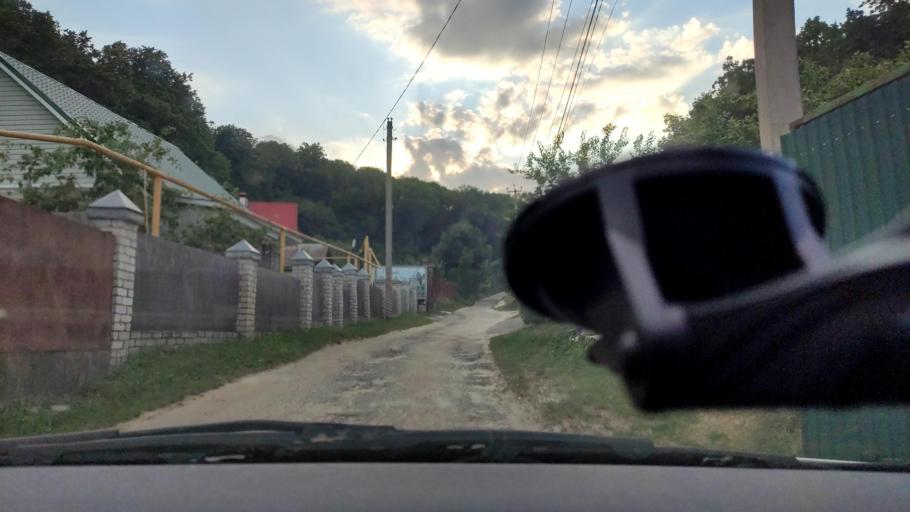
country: RU
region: Voronezj
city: Ramon'
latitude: 51.8954
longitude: 39.3398
